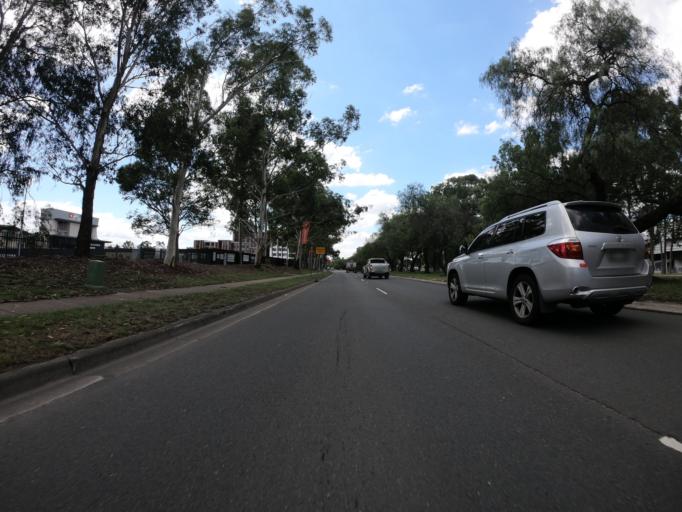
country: AU
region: New South Wales
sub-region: Penrith Municipality
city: Penrith
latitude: -33.7583
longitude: 150.6854
